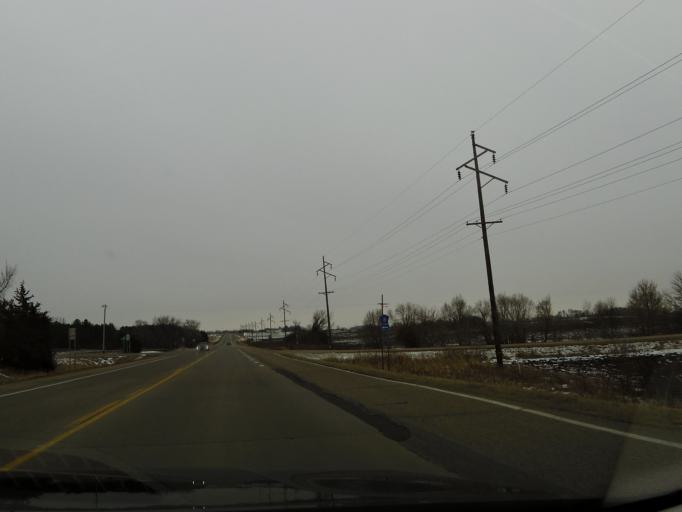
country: US
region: Minnesota
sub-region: Scott County
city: Jordan
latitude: 44.6313
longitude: -93.6116
